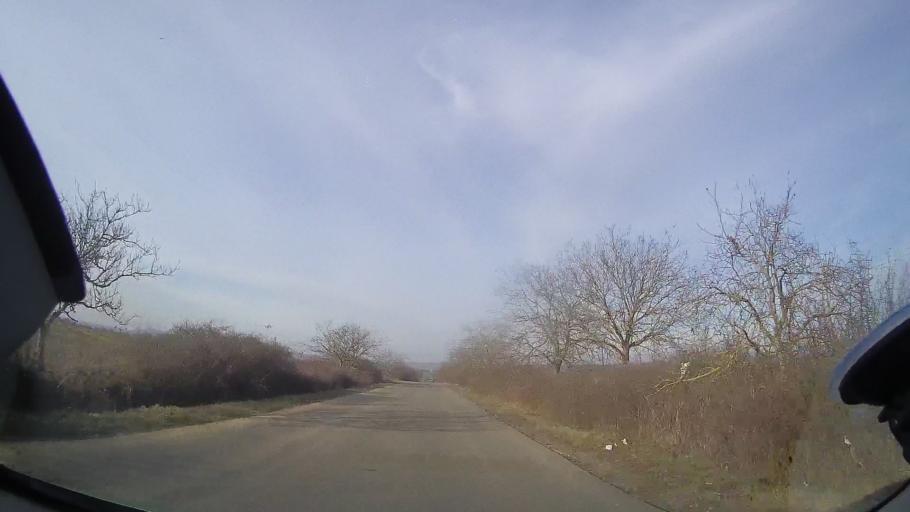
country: RO
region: Bihor
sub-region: Comuna Spinus
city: Spinus
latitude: 47.2238
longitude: 22.1694
